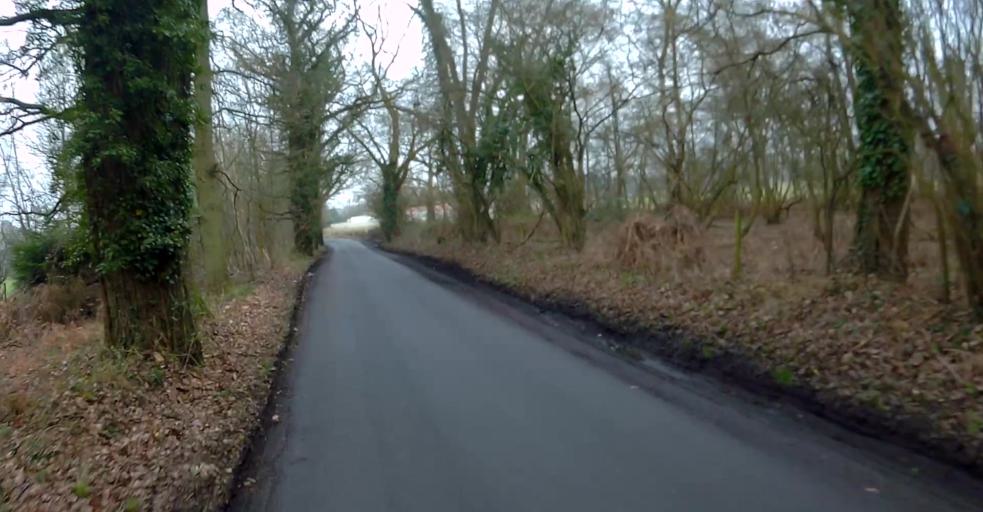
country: GB
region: England
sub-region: Hampshire
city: Eversley
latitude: 51.3652
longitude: -0.8906
